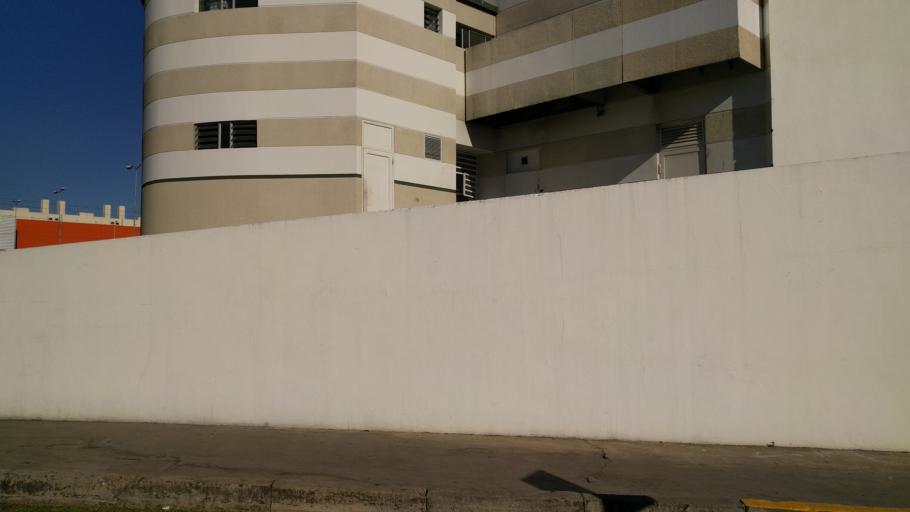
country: BO
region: Santa Cruz
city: Santa Cruz de la Sierra
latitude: -17.7724
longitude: -63.2040
